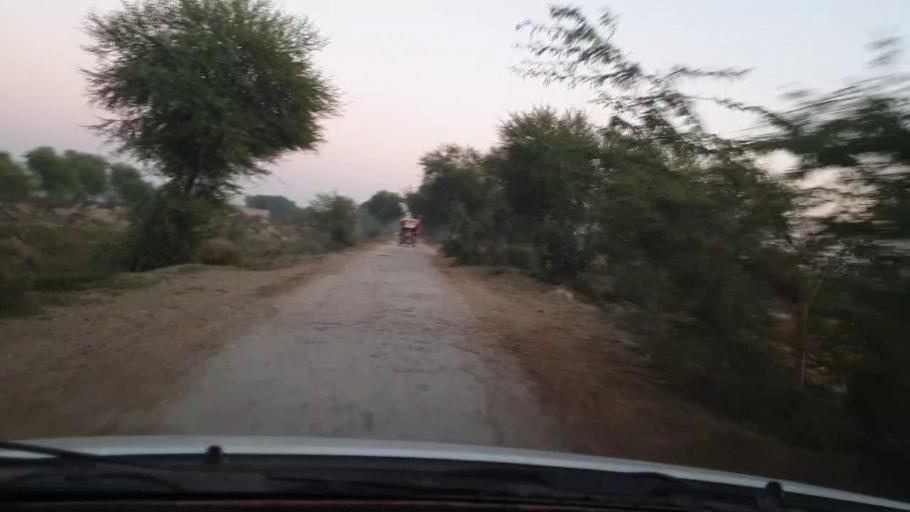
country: PK
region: Sindh
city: Khairpur Nathan Shah
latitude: 27.1492
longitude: 67.6962
